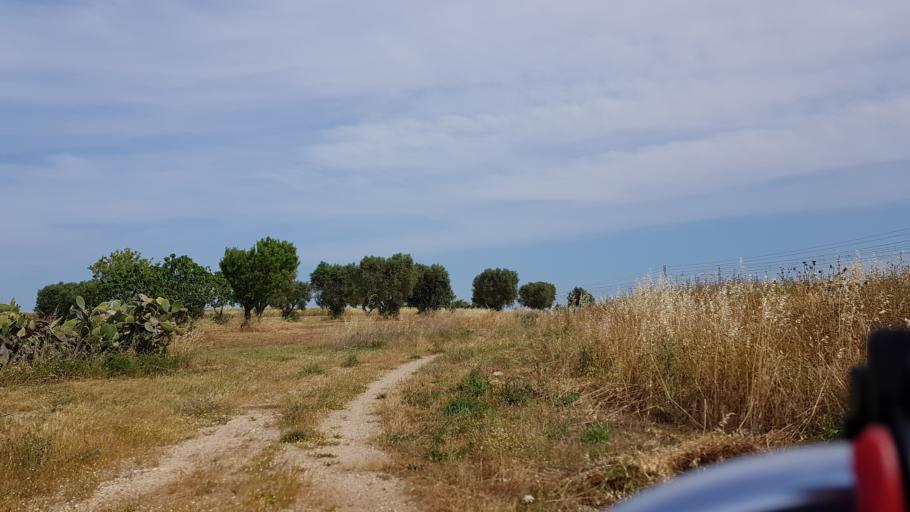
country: IT
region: Apulia
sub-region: Provincia di Brindisi
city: San Vito dei Normanni
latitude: 40.6584
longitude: 17.8026
